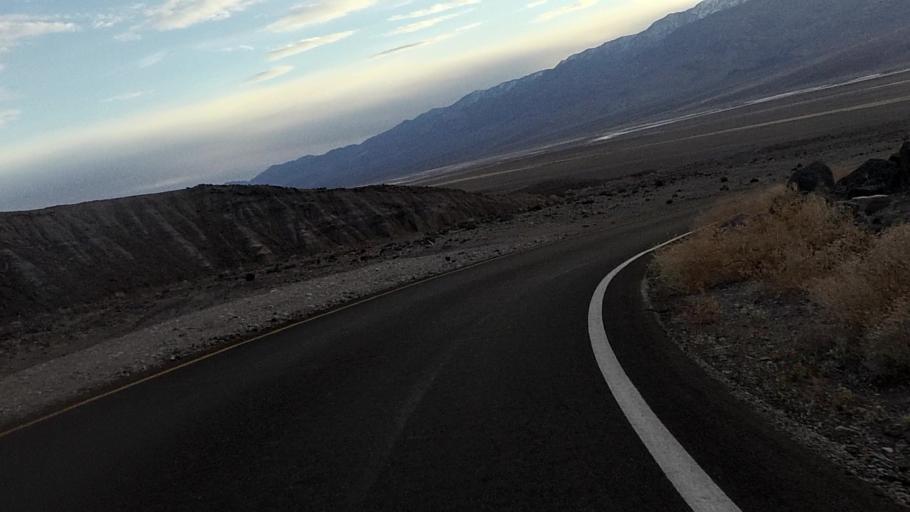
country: US
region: Nevada
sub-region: Nye County
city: Beatty
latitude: 36.3807
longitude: -116.8407
